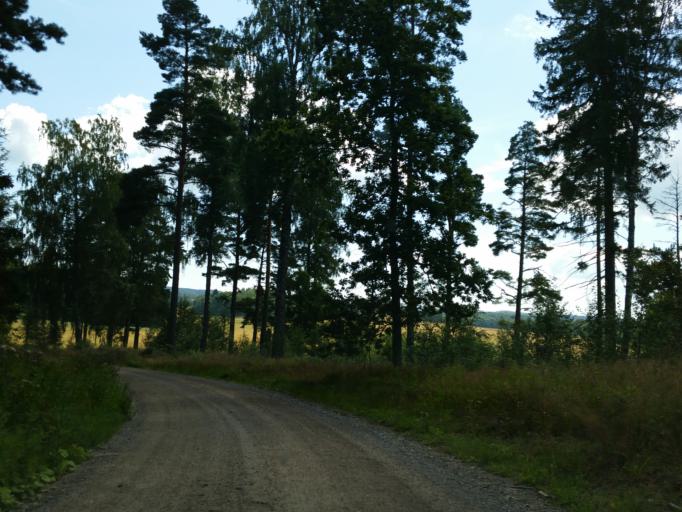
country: SE
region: Stockholm
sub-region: Sodertalje Kommun
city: Pershagen
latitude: 59.0588
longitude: 17.6546
